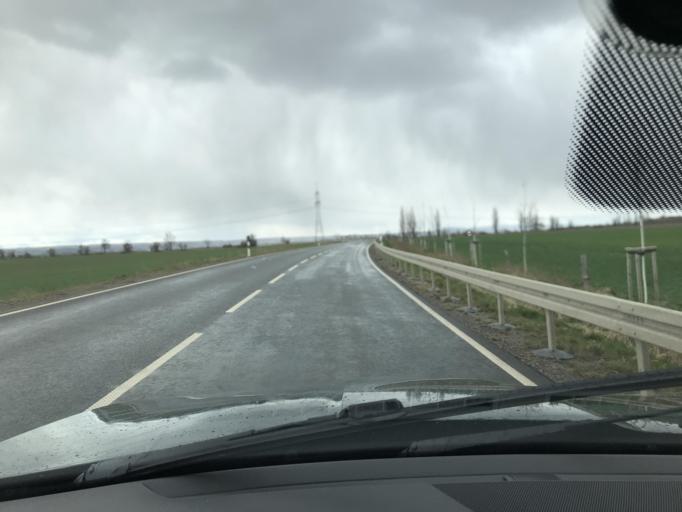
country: DE
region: Saxony-Anhalt
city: Hoym
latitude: 51.7691
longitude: 11.2924
